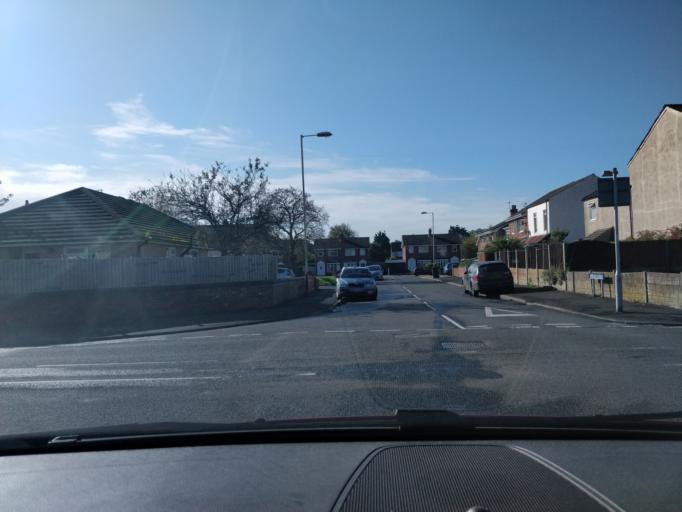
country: GB
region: England
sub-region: Sefton
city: Southport
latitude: 53.6412
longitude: -2.9775
